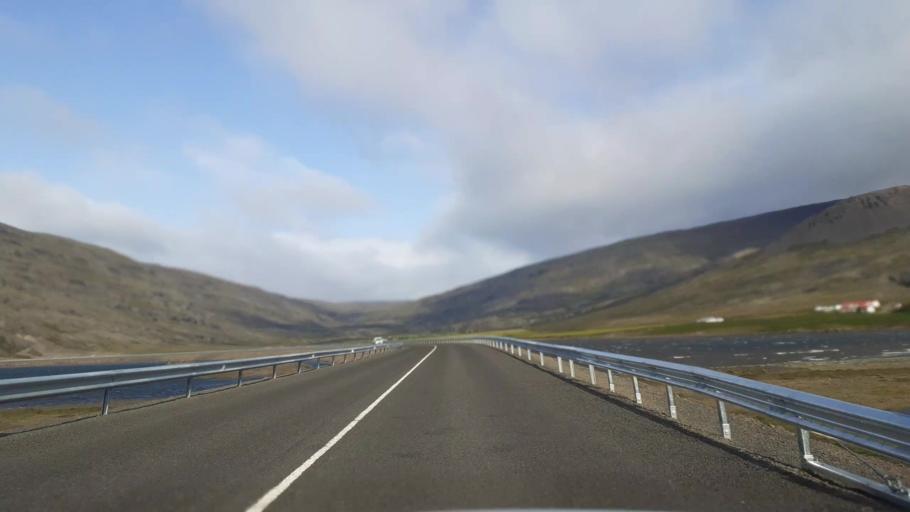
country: IS
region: East
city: Reydarfjoerdur
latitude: 64.7896
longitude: -14.4742
